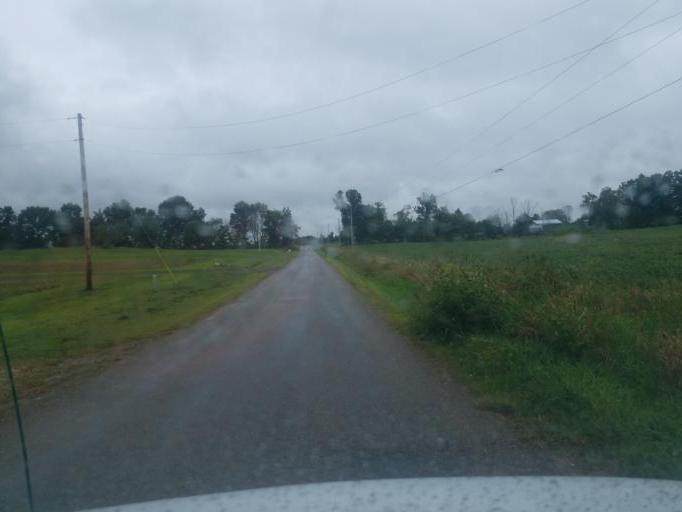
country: US
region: Ohio
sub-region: Wayne County
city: West Salem
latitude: 40.9211
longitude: -82.1186
